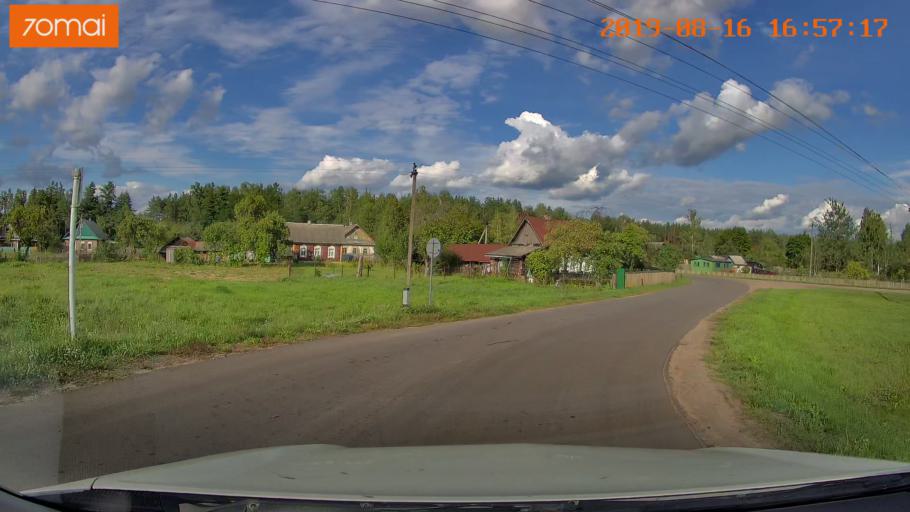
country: BY
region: Mogilev
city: Hlusha
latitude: 53.2574
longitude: 28.8245
